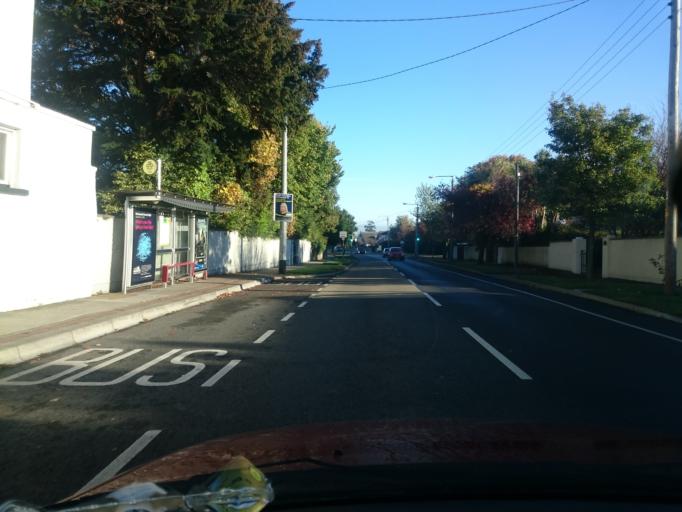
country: IE
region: Leinster
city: Foxrock
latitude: 53.2833
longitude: -6.1789
